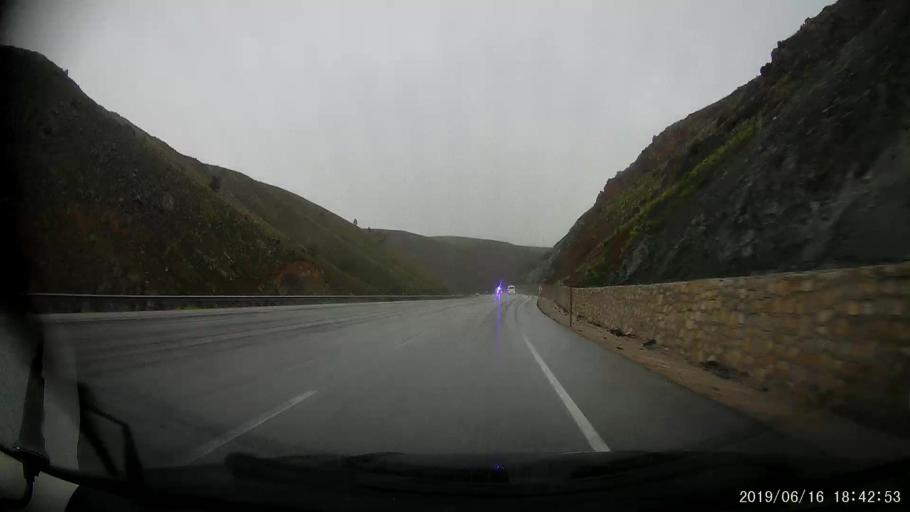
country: TR
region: Erzincan
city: Doganbeyli
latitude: 39.8679
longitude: 39.1000
